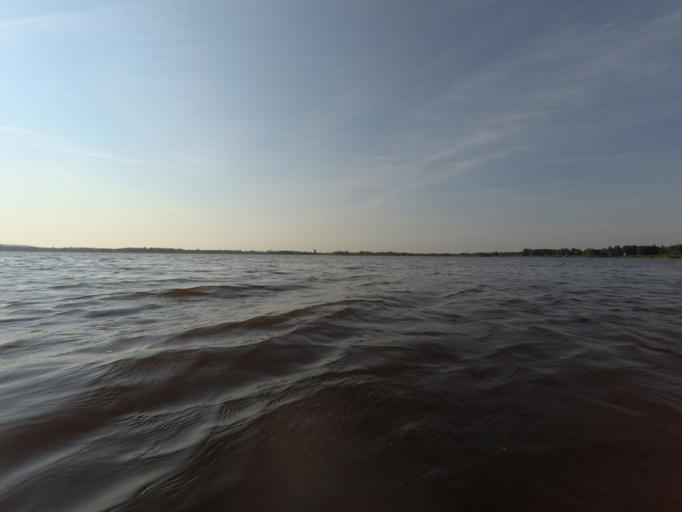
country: NL
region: Overijssel
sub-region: Gemeente Steenwijkerland
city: Wanneperveen
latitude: 52.6690
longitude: 6.0759
